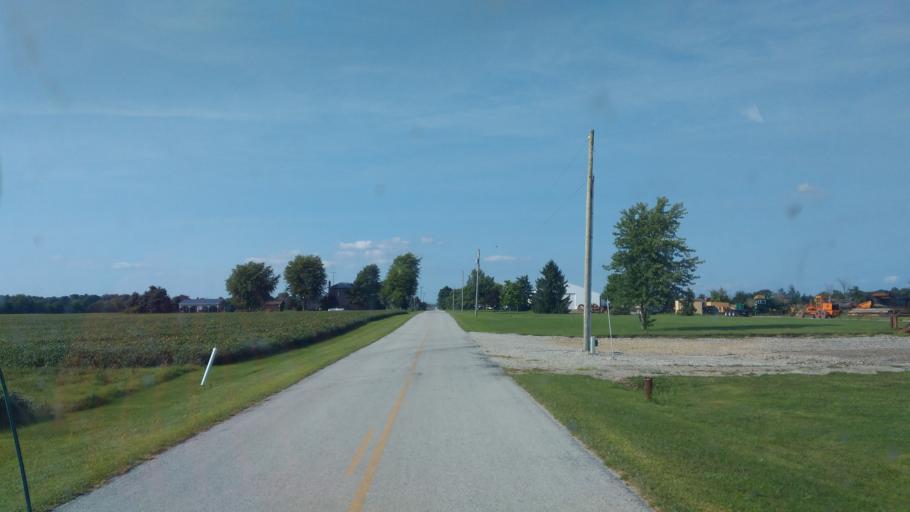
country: US
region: Ohio
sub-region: Hardin County
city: Forest
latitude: 40.7422
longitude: -83.5763
